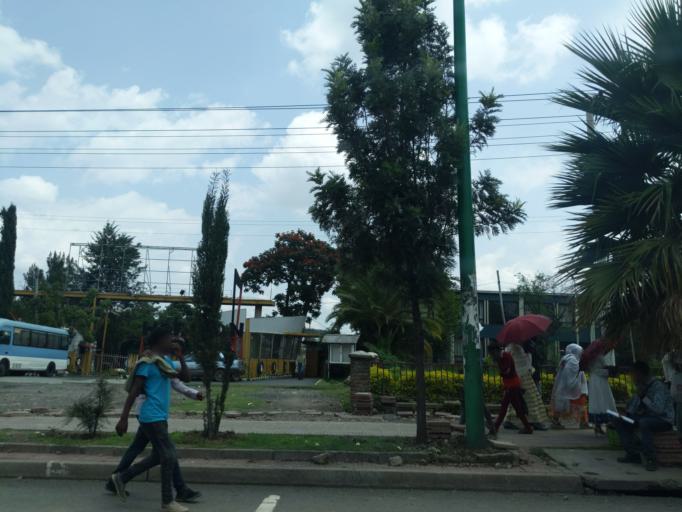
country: ET
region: Adis Abeba
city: Addis Ababa
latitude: 8.9493
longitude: 38.7641
